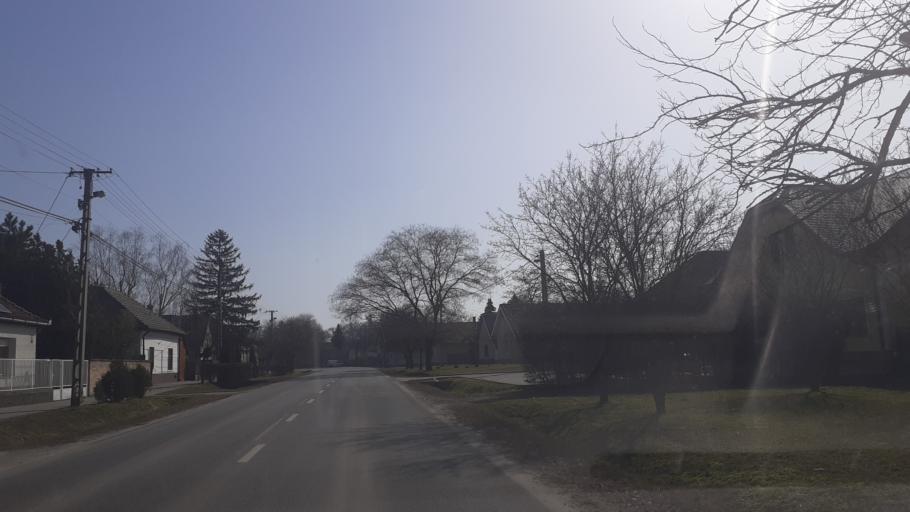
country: HU
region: Pest
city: Dabas
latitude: 47.1683
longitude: 19.3260
